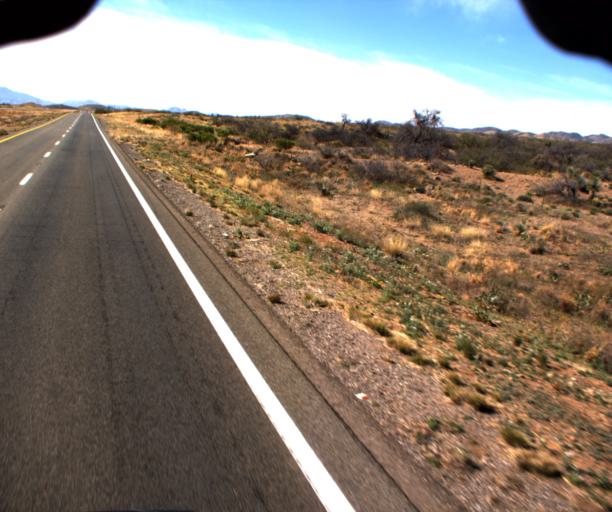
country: US
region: Arizona
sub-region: Graham County
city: Swift Trail Junction
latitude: 32.4940
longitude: -109.6738
